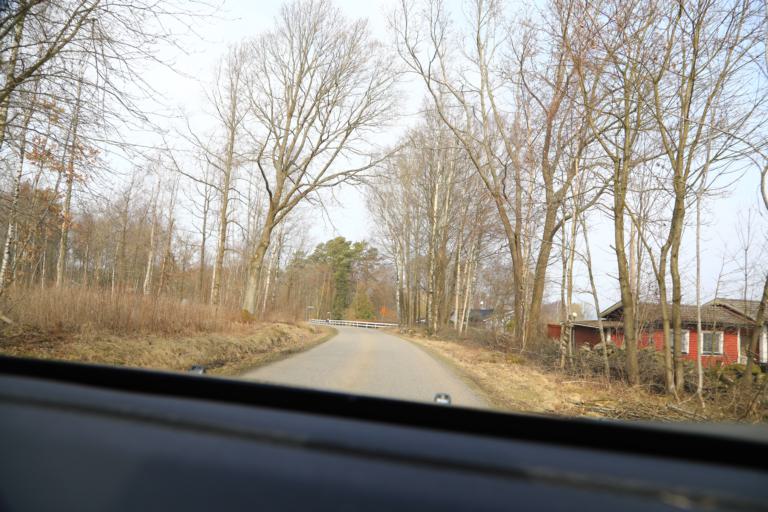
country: SE
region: Halland
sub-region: Kungsbacka Kommun
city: Frillesas
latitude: 57.2773
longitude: 12.1412
